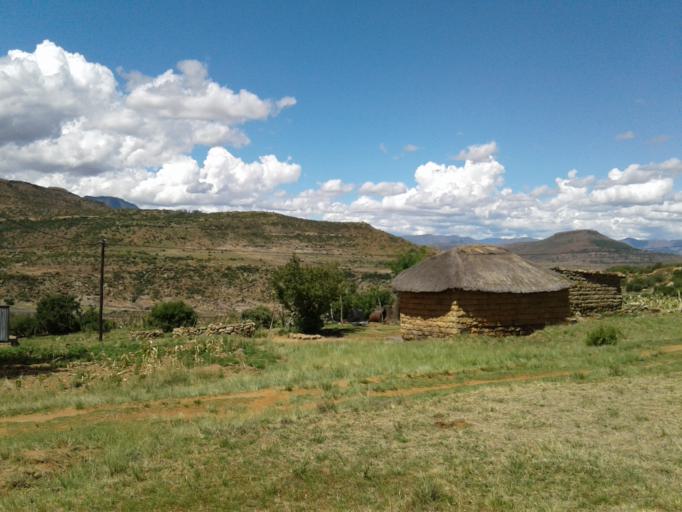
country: LS
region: Quthing
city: Quthing
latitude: -30.3689
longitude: 27.5491
